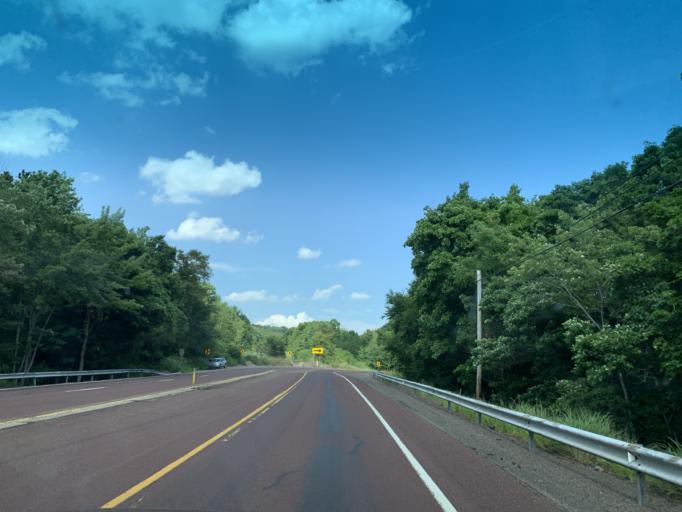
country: US
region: Pennsylvania
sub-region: Schuylkill County
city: Ashland
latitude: 40.7912
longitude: -76.3495
